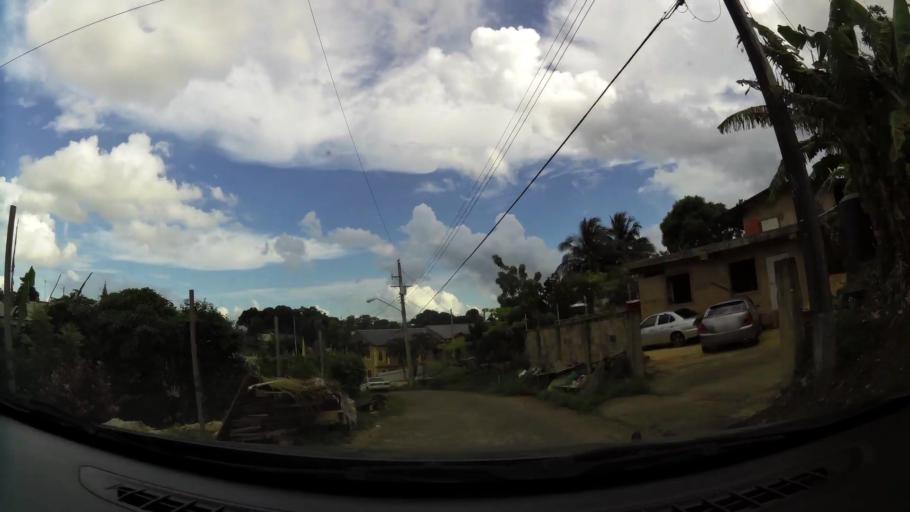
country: TT
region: City of San Fernando
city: Mon Repos
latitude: 10.2698
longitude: -61.4518
